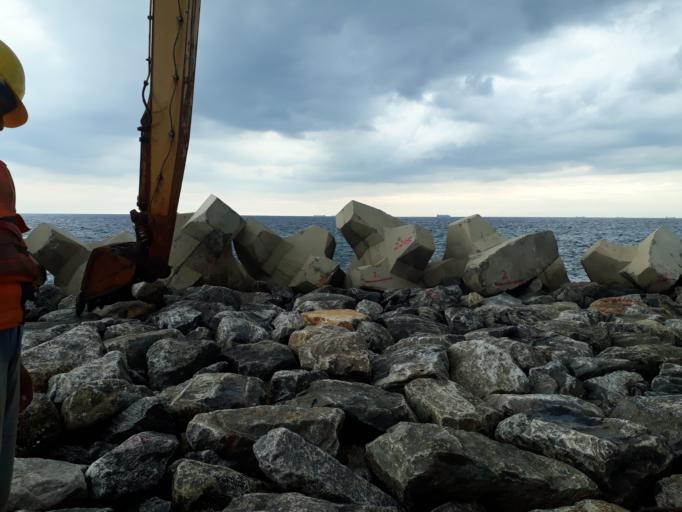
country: LK
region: Western
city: Colombo
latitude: 6.9311
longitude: 79.8207
